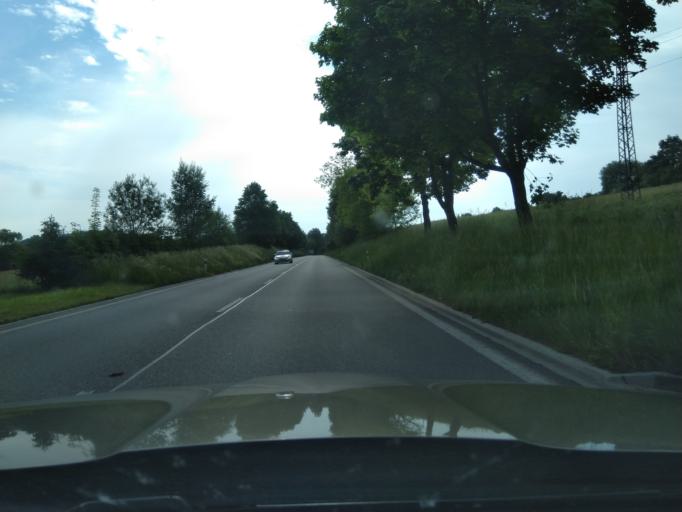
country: CZ
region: Jihocesky
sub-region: Okres Prachatice
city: Strunkovice nad Blanici
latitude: 49.0564
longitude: 14.0855
